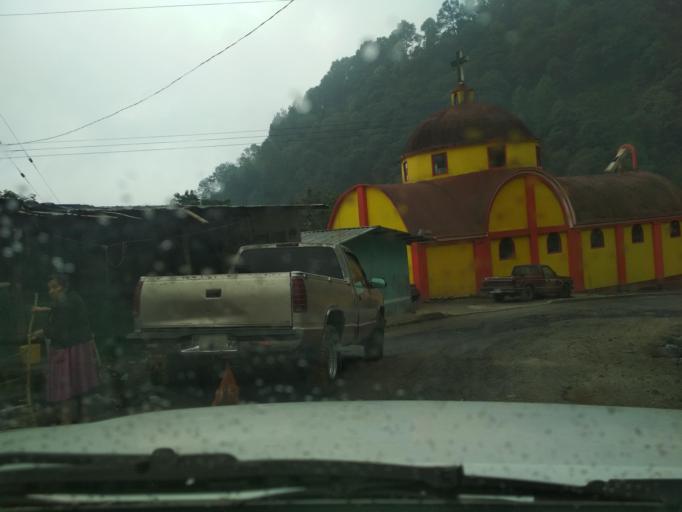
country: MX
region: Veracruz
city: La Perla
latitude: 18.9395
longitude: -97.1490
